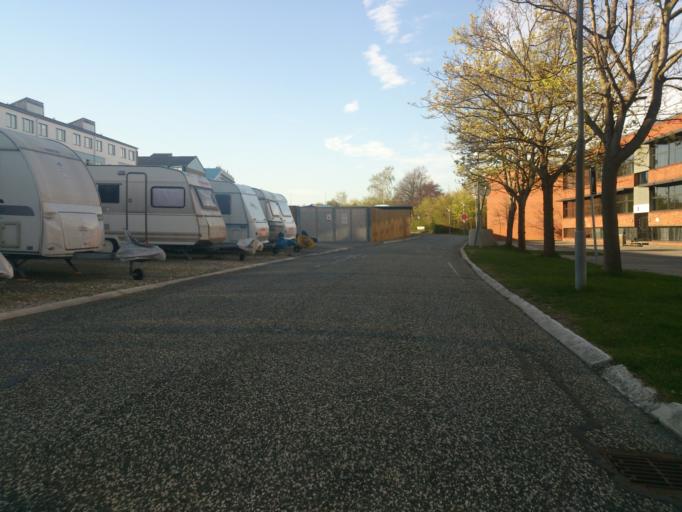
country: DK
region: Capital Region
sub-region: Ballerup Kommune
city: Ballerup
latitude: 55.7309
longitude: 12.3510
